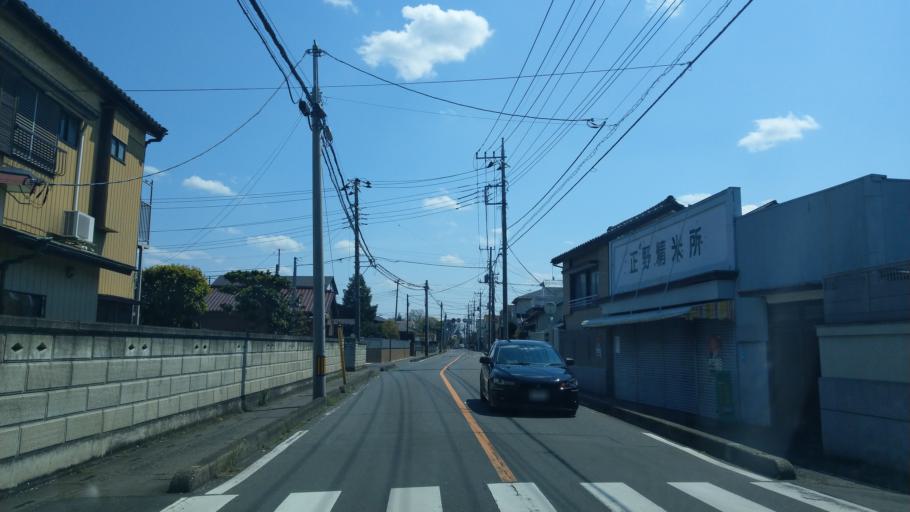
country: JP
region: Saitama
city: Yono
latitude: 35.8907
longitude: 139.6094
